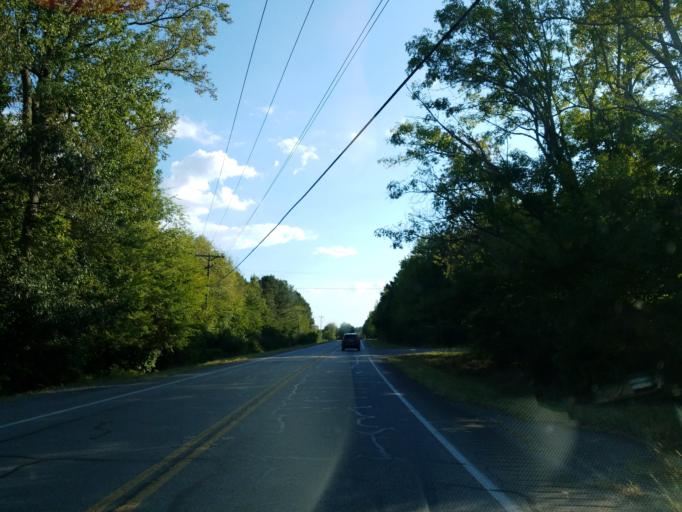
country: US
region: Georgia
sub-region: Murray County
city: Chatsworth
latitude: 34.9073
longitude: -84.7464
